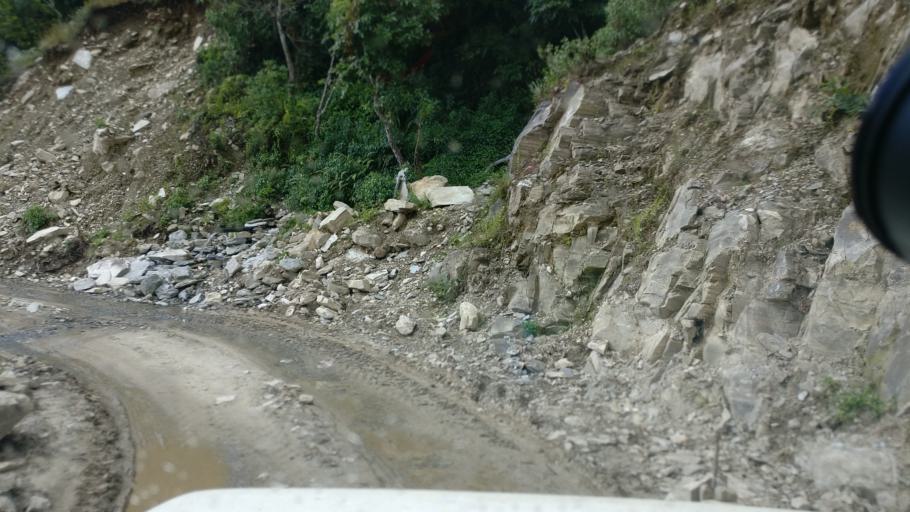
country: NP
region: Western Region
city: Baglung
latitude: 28.2746
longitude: 83.6436
